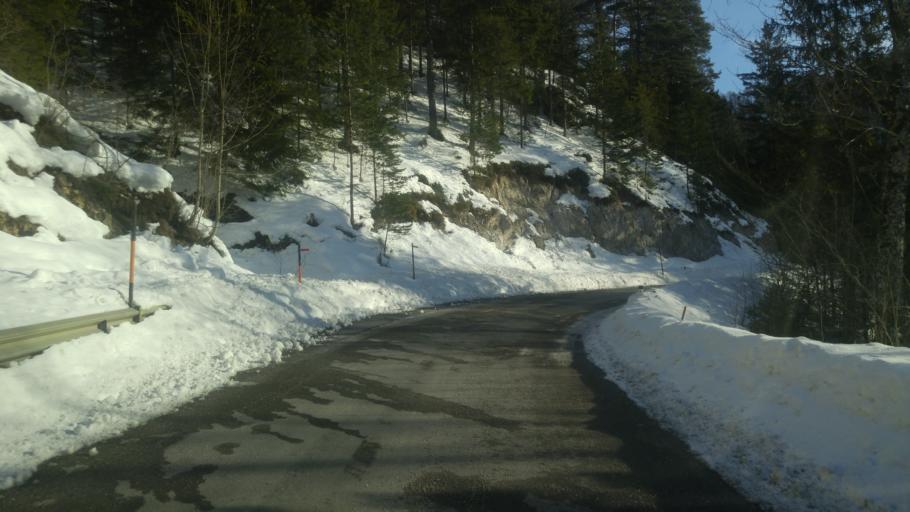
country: AT
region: Lower Austria
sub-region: Politischer Bezirk Lilienfeld
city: Hohenberg
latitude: 47.8830
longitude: 15.6231
